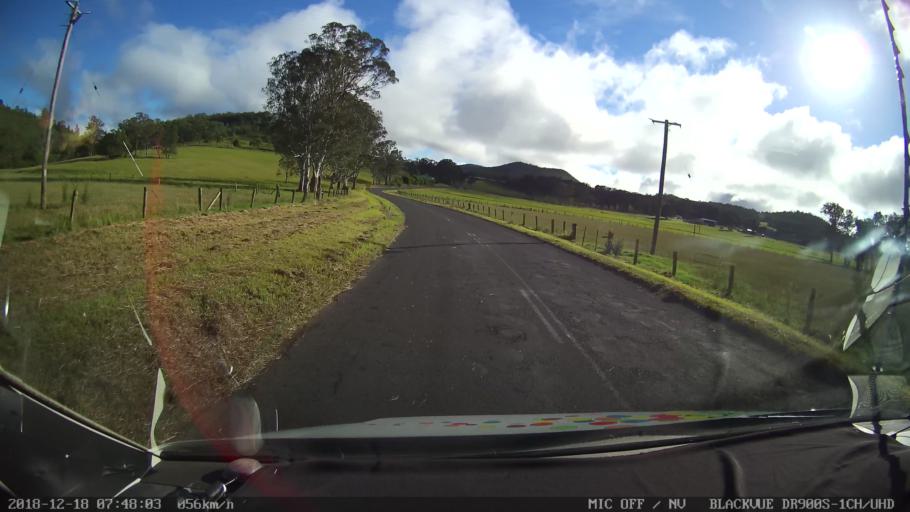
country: AU
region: New South Wales
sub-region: Kyogle
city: Kyogle
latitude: -28.4611
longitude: 152.5622
